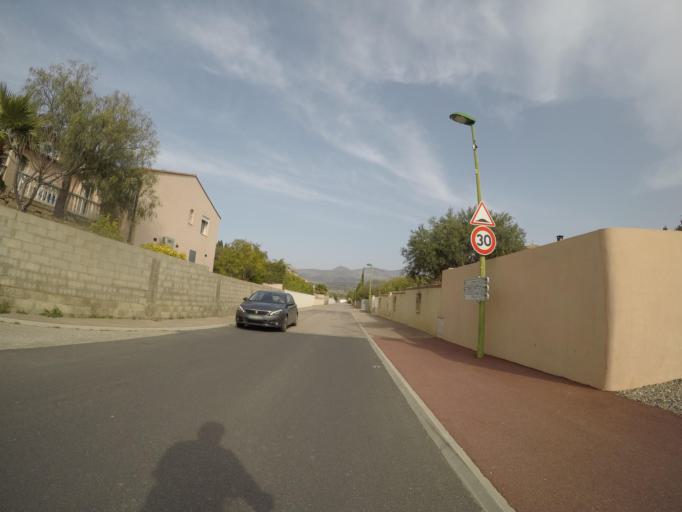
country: FR
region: Languedoc-Roussillon
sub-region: Departement des Pyrenees-Orientales
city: Baixas
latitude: 42.7734
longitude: 2.7960
